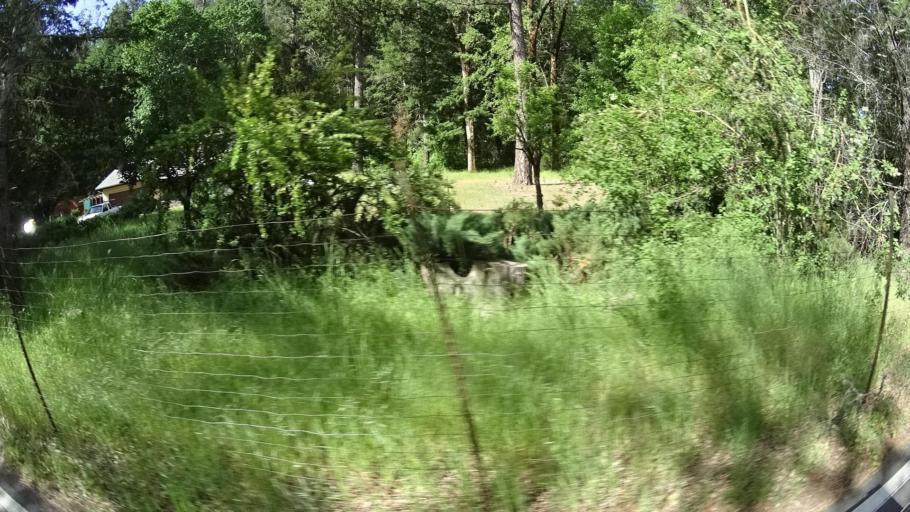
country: US
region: California
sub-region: Lake County
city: Cobb
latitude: 38.8971
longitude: -122.7401
